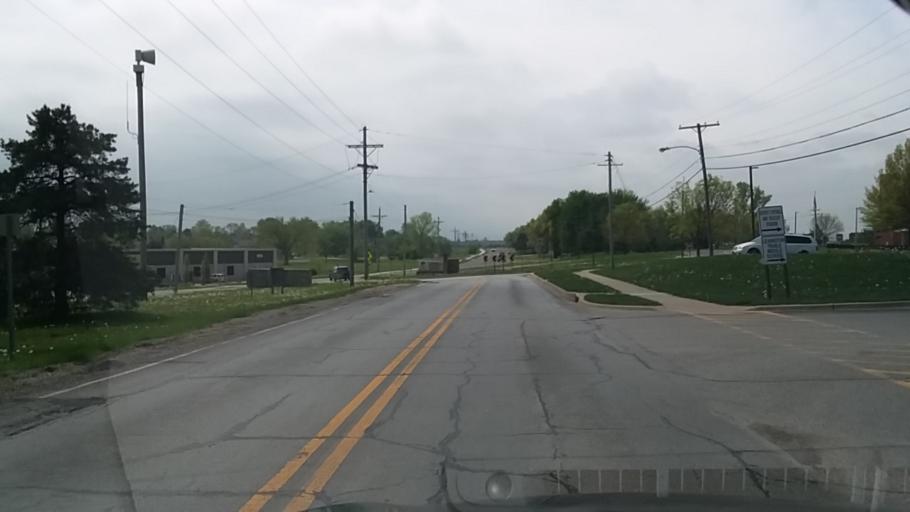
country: US
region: Kansas
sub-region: Johnson County
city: De Soto
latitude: 38.9696
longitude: -94.9832
